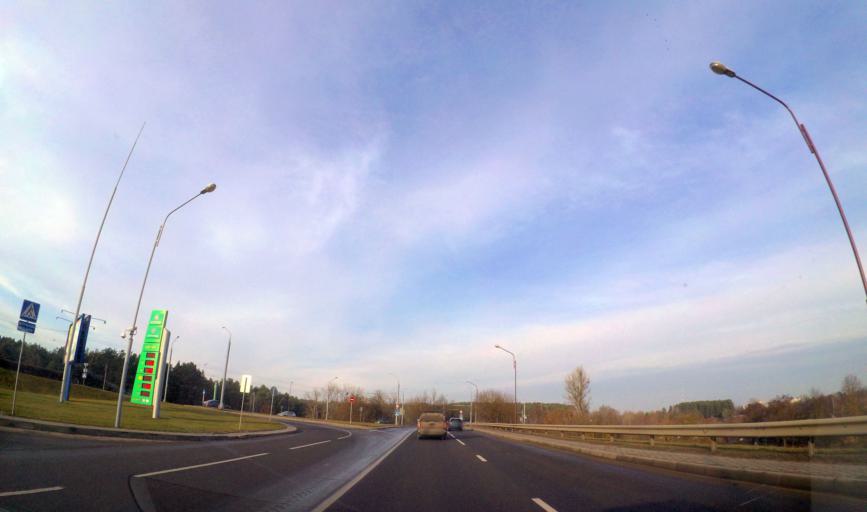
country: BY
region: Grodnenskaya
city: Hrodna
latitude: 53.6761
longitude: 23.8058
